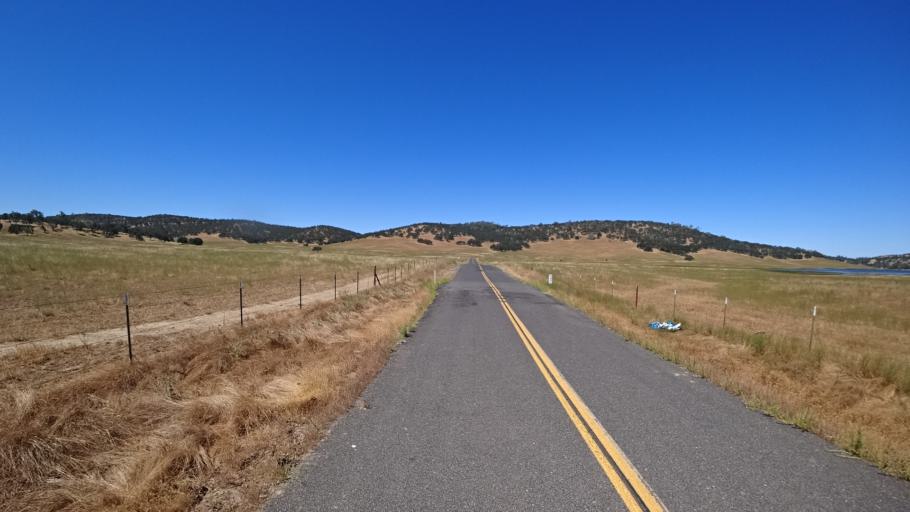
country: US
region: California
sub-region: Calaveras County
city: Copperopolis
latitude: 38.0208
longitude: -120.7443
